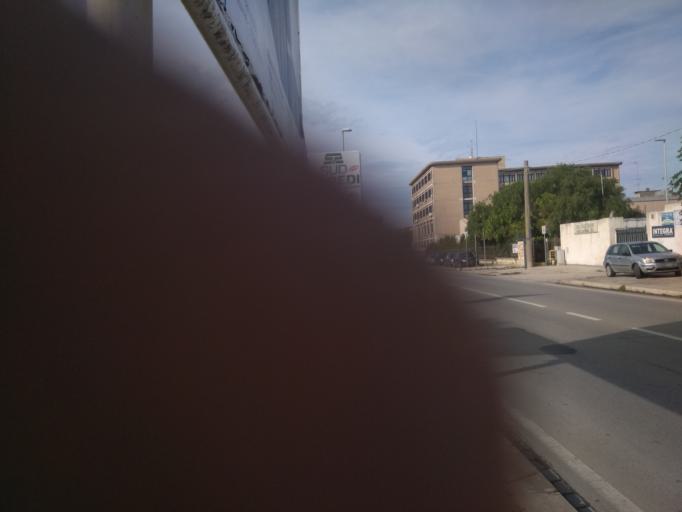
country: IT
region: Apulia
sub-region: Provincia di Bari
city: Bari
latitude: 41.1121
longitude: 16.9007
